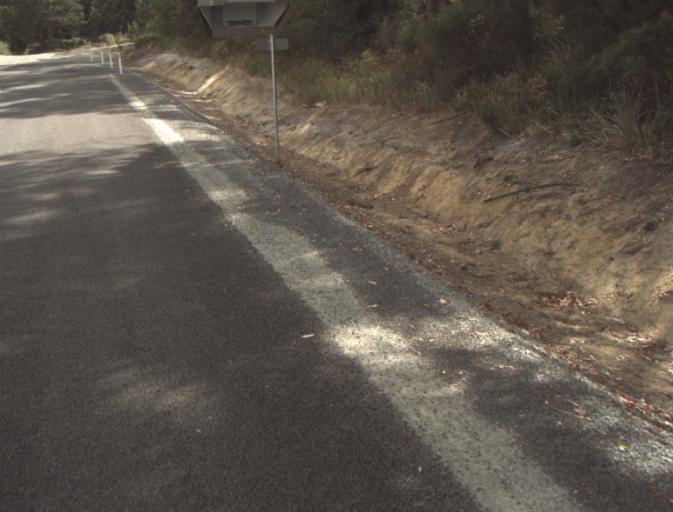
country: AU
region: Tasmania
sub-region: Launceston
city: Mayfield
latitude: -41.2190
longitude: 147.2065
